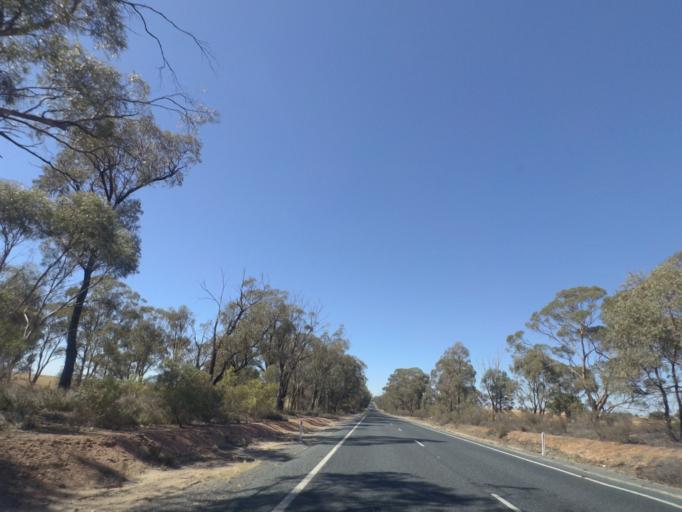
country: AU
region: New South Wales
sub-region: Bland
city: West Wyalong
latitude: -34.1465
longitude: 147.1192
